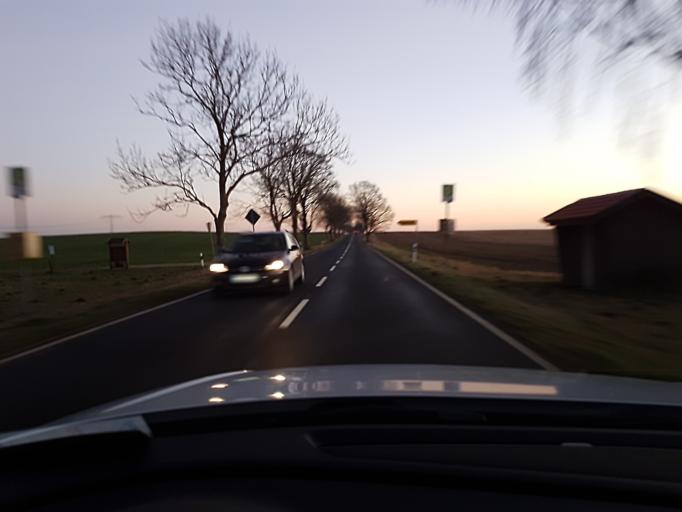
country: DE
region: Mecklenburg-Vorpommern
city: Gingst
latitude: 54.5006
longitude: 13.2794
